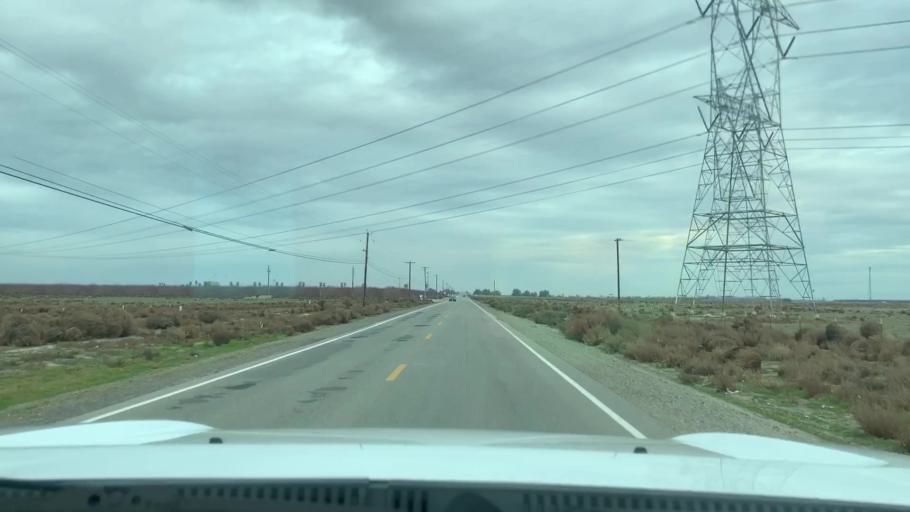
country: US
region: California
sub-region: Kern County
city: Rosedale
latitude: 35.2792
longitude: -119.2526
